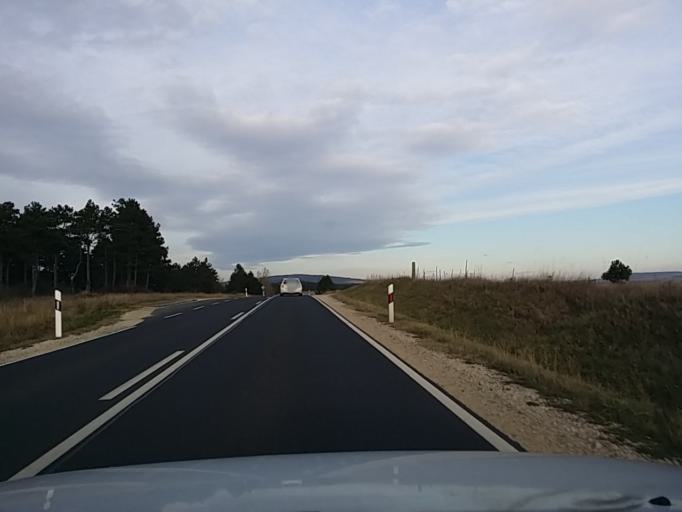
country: HU
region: Veszprem
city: Herend
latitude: 47.0039
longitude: 17.7466
